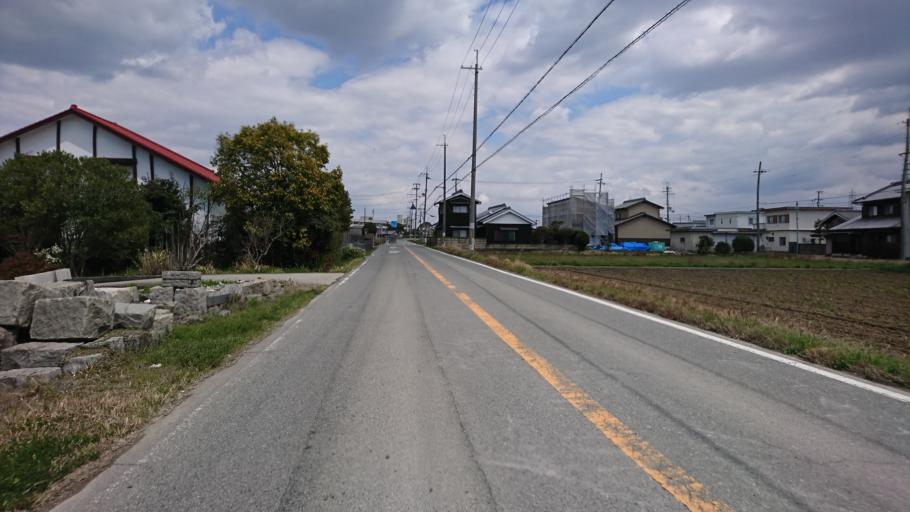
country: JP
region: Hyogo
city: Miki
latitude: 34.7511
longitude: 134.9401
